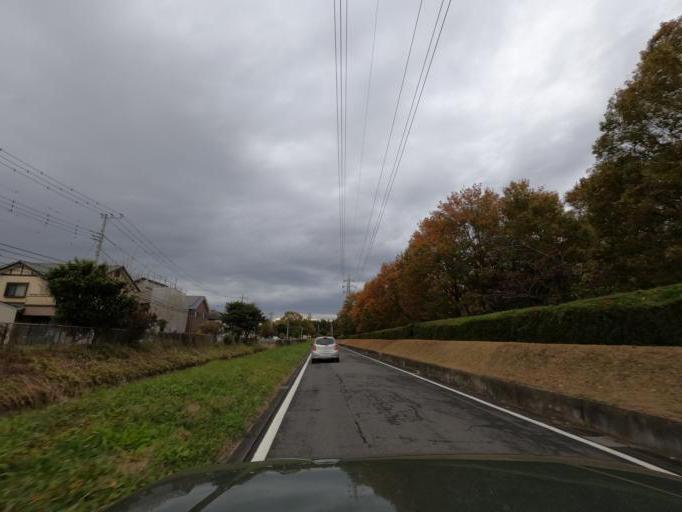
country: JP
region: Ibaraki
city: Tsukuba
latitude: 36.1241
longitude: 140.0891
